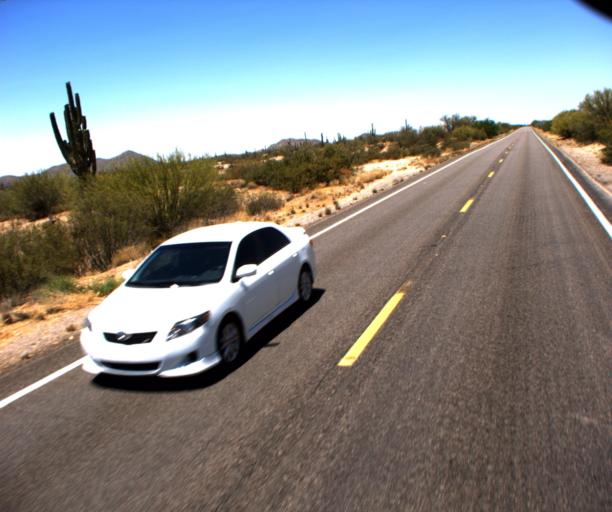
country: US
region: Arizona
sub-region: Pima County
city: Catalina
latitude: 32.7112
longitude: -111.1005
